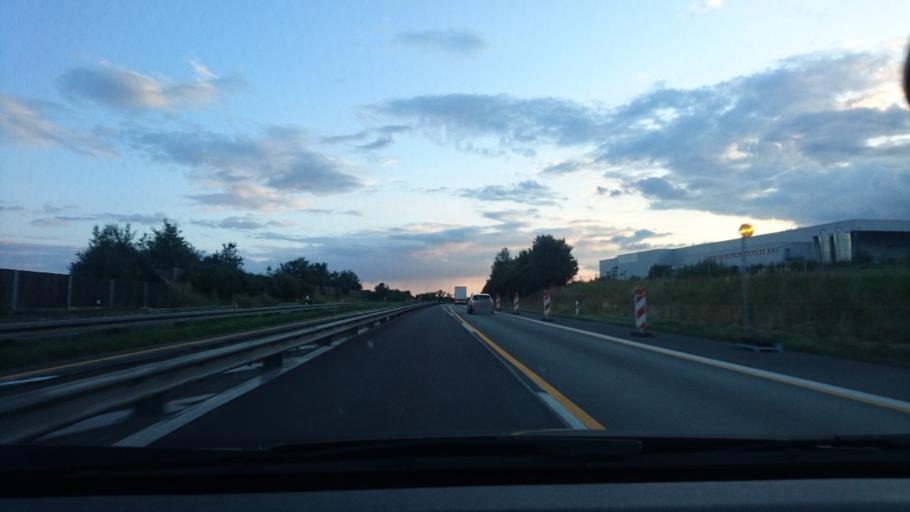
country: DE
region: Saxony
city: Treuen
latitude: 50.5431
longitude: 12.2634
